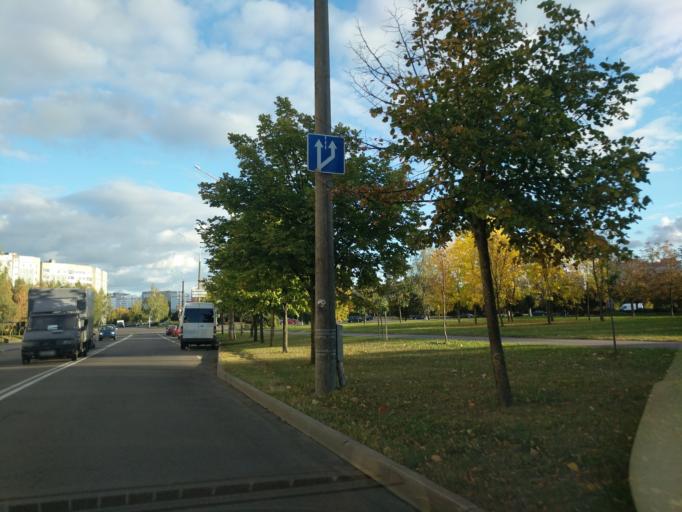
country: BY
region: Minsk
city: Malinovka
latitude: 53.8581
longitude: 27.4545
